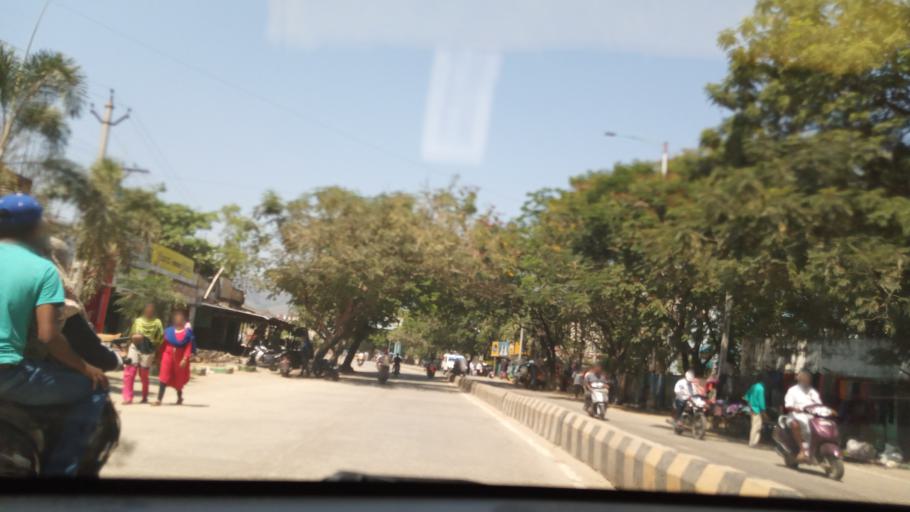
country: IN
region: Andhra Pradesh
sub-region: Chittoor
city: Tirupati
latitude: 13.6187
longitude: 79.4174
